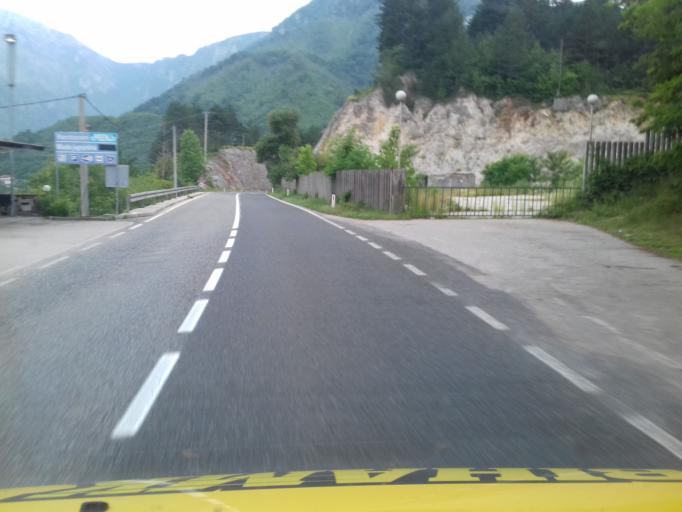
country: BA
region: Federation of Bosnia and Herzegovina
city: Jablanica
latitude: 43.6299
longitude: 17.7534
